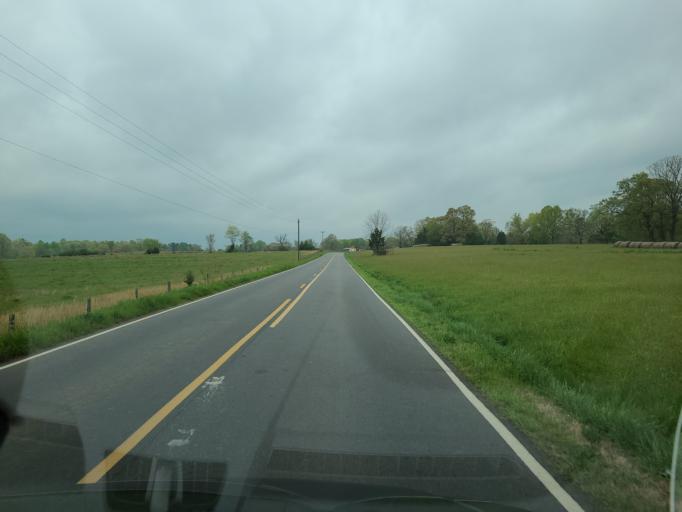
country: US
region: North Carolina
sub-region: Gaston County
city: Cherryville
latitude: 35.4304
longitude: -81.4309
